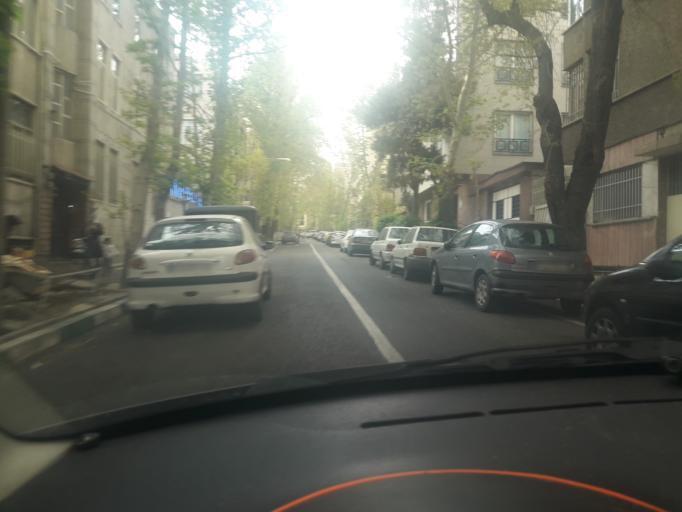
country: IR
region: Tehran
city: Tehran
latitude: 35.7383
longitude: 51.4074
